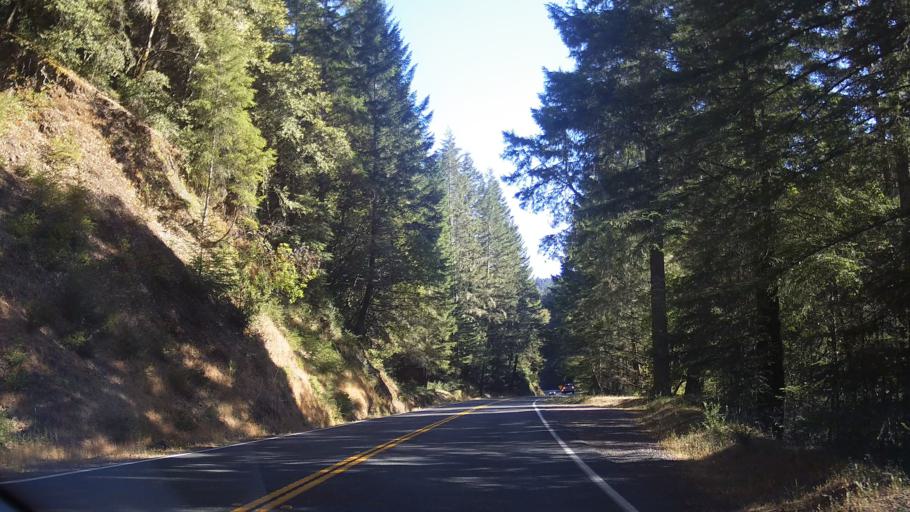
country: US
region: California
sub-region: Mendocino County
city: Brooktrails
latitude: 39.3563
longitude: -123.5094
